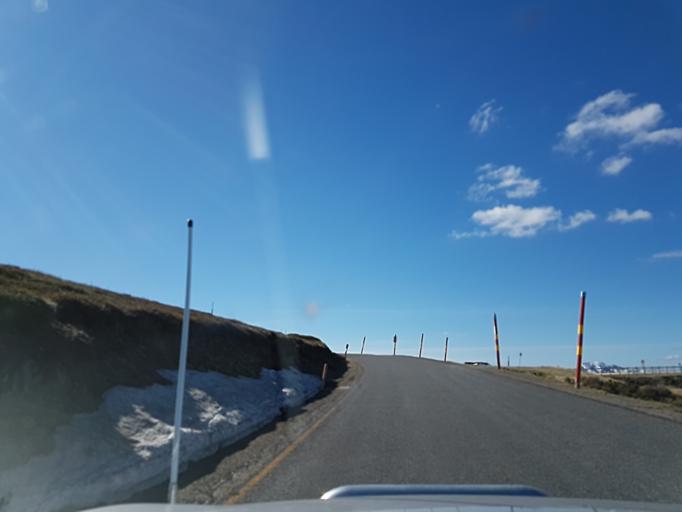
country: AU
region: Victoria
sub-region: Alpine
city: Mount Beauty
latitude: -36.9758
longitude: 147.1384
